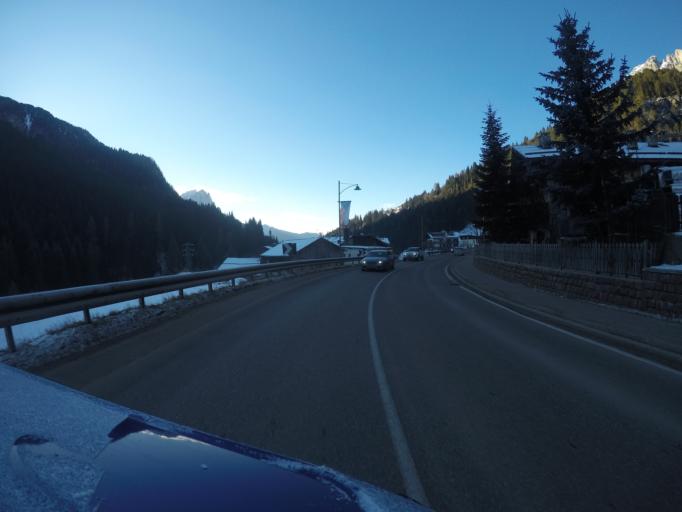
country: IT
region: Trentino-Alto Adige
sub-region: Provincia di Trento
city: Mazzin
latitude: 46.4572
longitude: 11.7012
